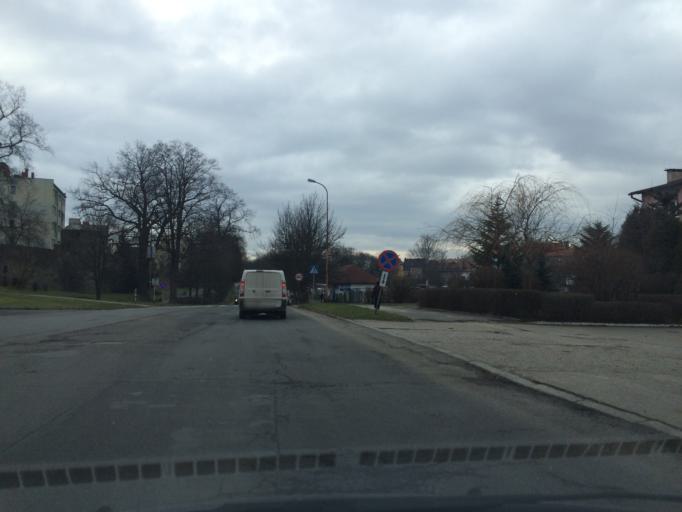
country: PL
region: Lower Silesian Voivodeship
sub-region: Powiat lubanski
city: Luban
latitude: 51.1230
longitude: 15.2918
